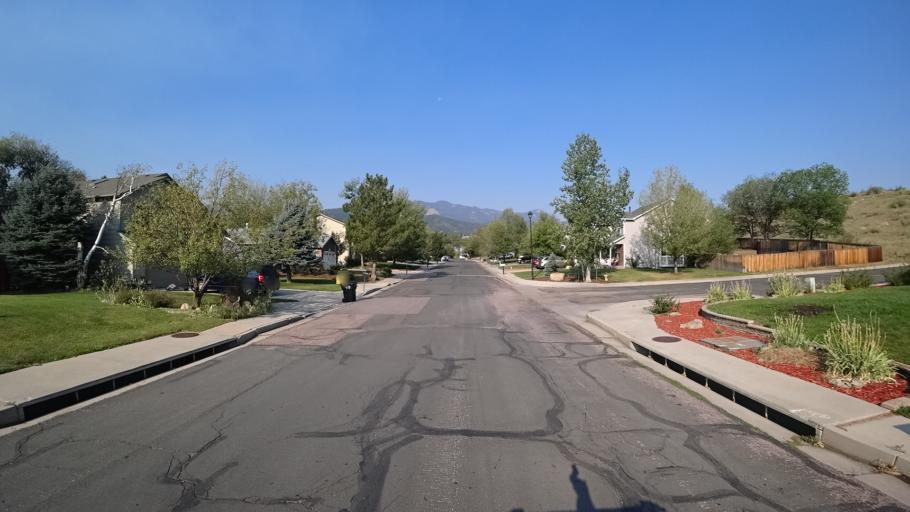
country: US
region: Colorado
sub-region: El Paso County
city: Colorado Springs
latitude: 38.8142
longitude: -104.8471
